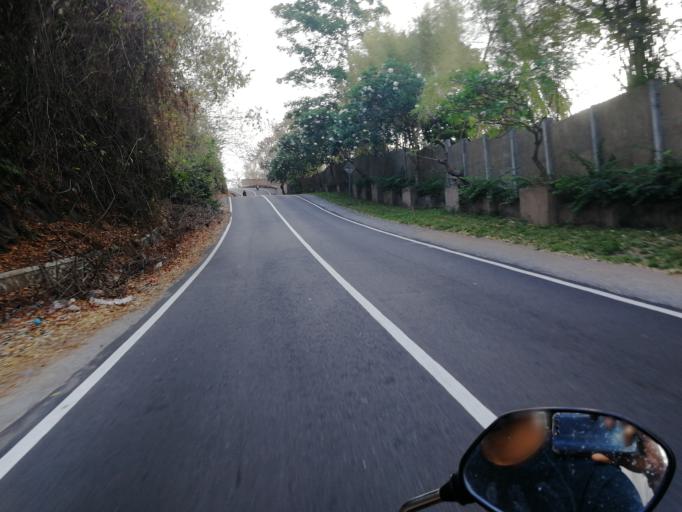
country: ID
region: West Nusa Tenggara
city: Karangsubagan
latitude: -8.4692
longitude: 116.0384
